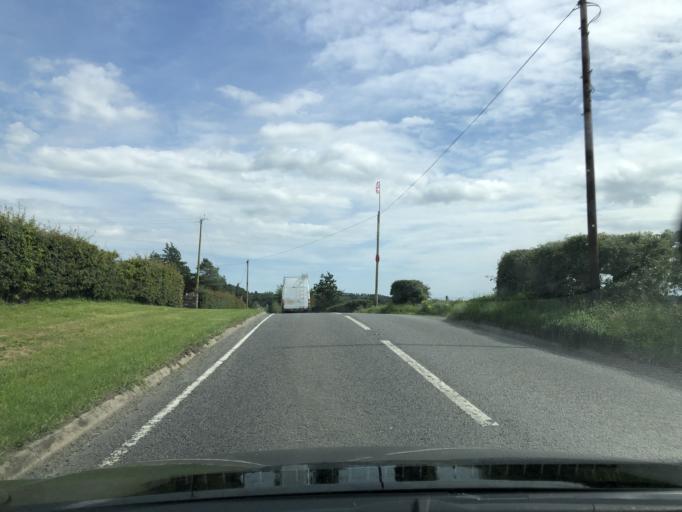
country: GB
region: Northern Ireland
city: Ballynahinch
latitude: 54.4207
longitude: -5.9159
